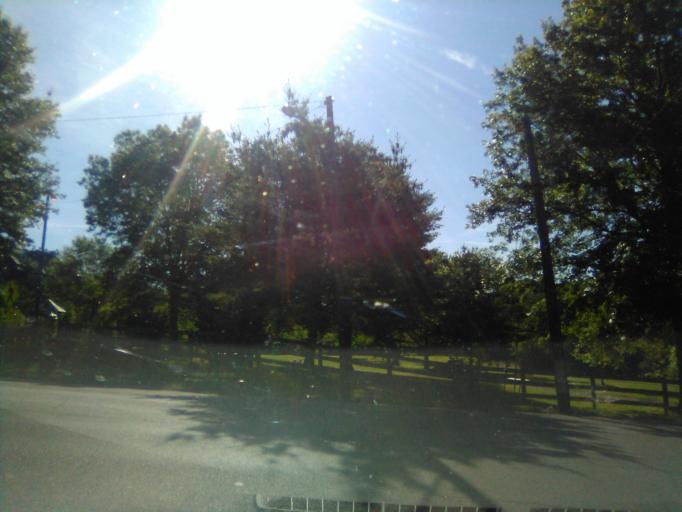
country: US
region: Tennessee
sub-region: Davidson County
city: Belle Meade
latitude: 36.1185
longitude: -86.8362
